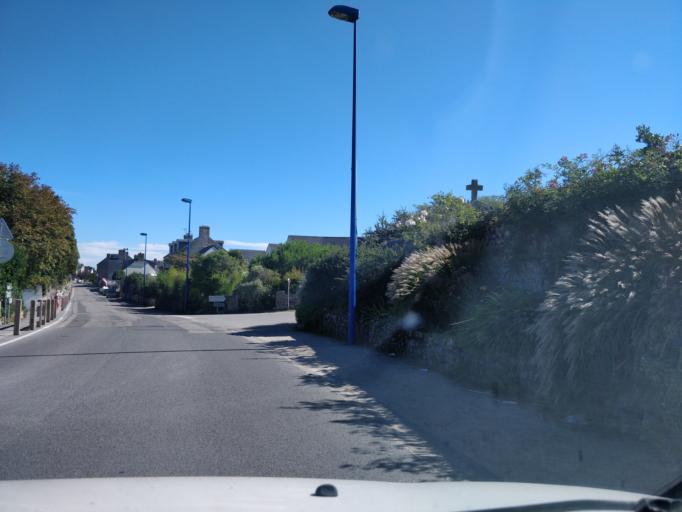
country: FR
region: Brittany
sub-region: Departement du Morbihan
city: Locmariaquer
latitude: 47.5712
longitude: -2.9477
